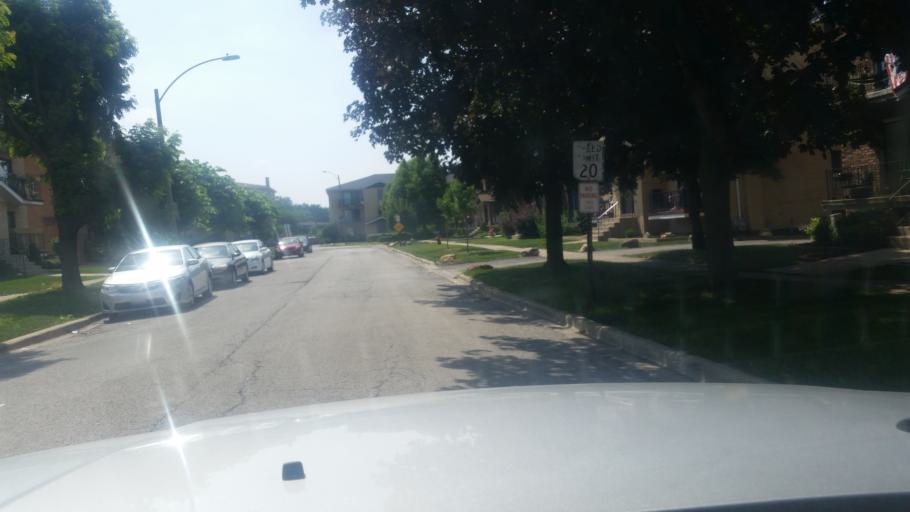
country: US
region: Illinois
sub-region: Cook County
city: Oak Lawn
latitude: 41.6997
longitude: -87.7627
